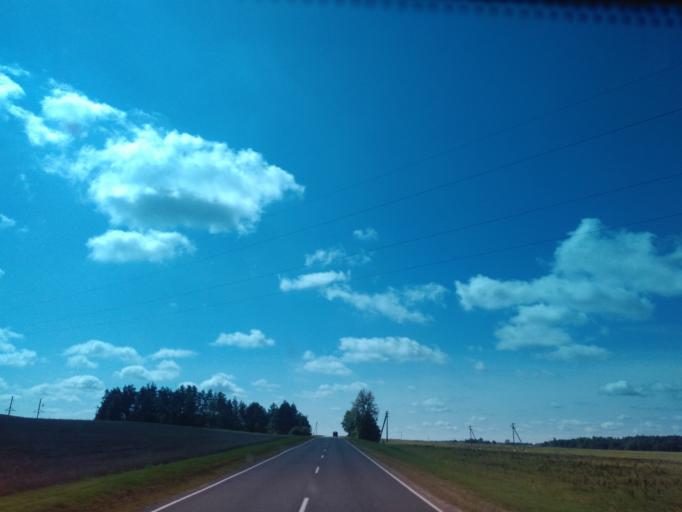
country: BY
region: Minsk
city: Uzda
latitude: 53.3843
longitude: 27.2418
